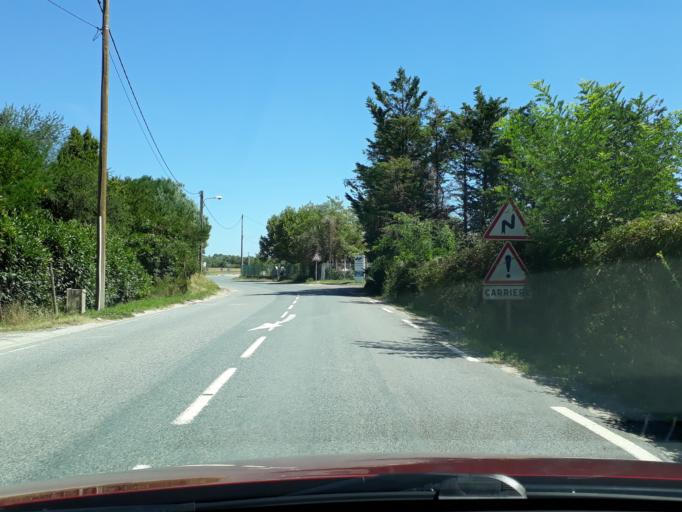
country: FR
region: Rhone-Alpes
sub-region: Departement du Rhone
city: Saint-Pierre-de-Chandieu
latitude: 45.6692
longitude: 5.0084
